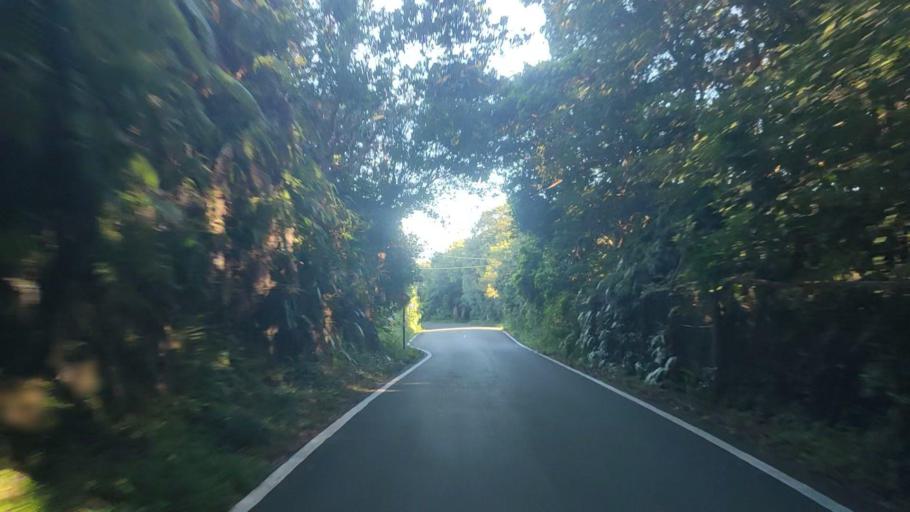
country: JP
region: Mie
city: Ise
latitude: 34.2658
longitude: 136.7702
